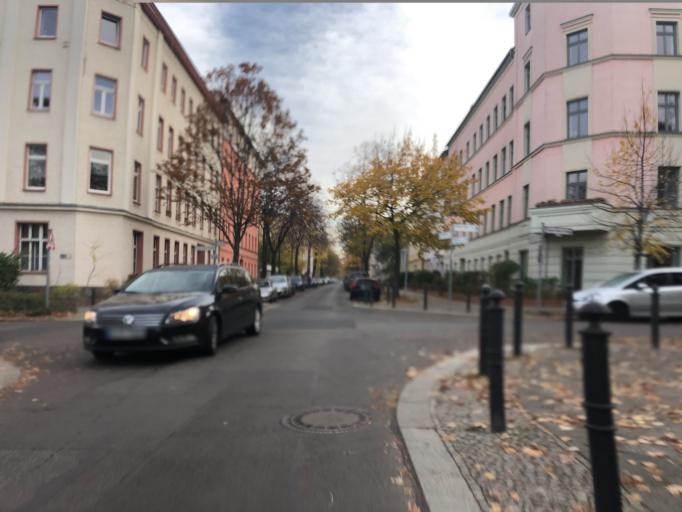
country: DE
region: Berlin
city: Weissensee
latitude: 52.5474
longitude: 13.4566
